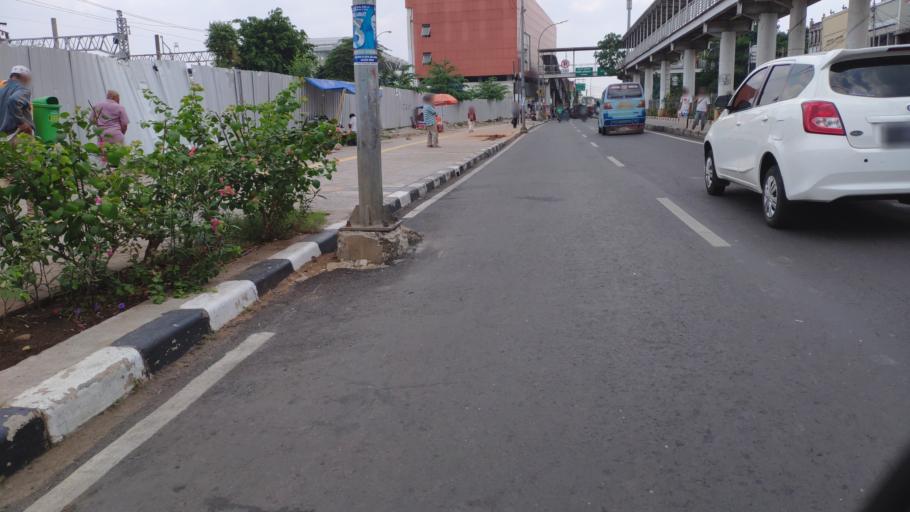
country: ID
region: Jakarta Raya
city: Jakarta
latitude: -6.2155
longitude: 106.8685
